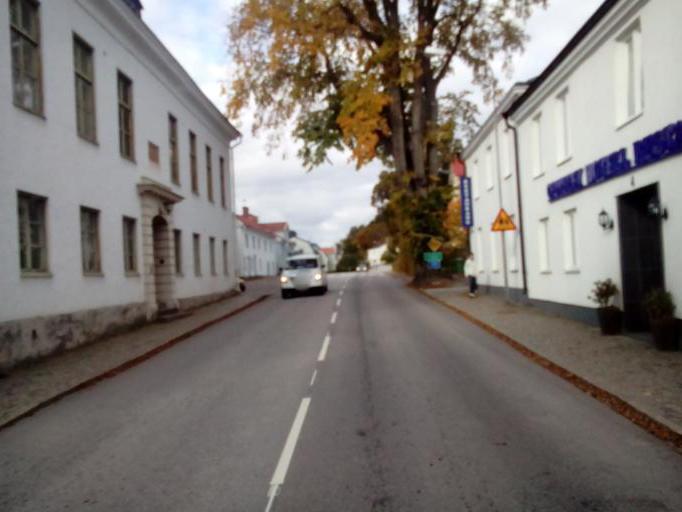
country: SE
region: Kalmar
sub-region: Vasterviks Kommun
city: Gamleby
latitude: 57.8999
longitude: 16.4076
